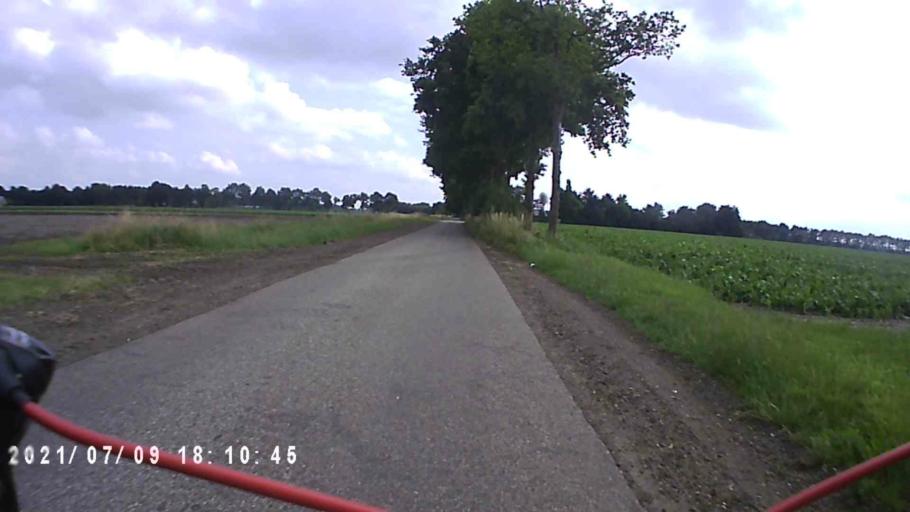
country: NL
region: Groningen
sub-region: Gemeente Pekela
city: Oude Pekela
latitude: 53.0707
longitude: 7.0321
